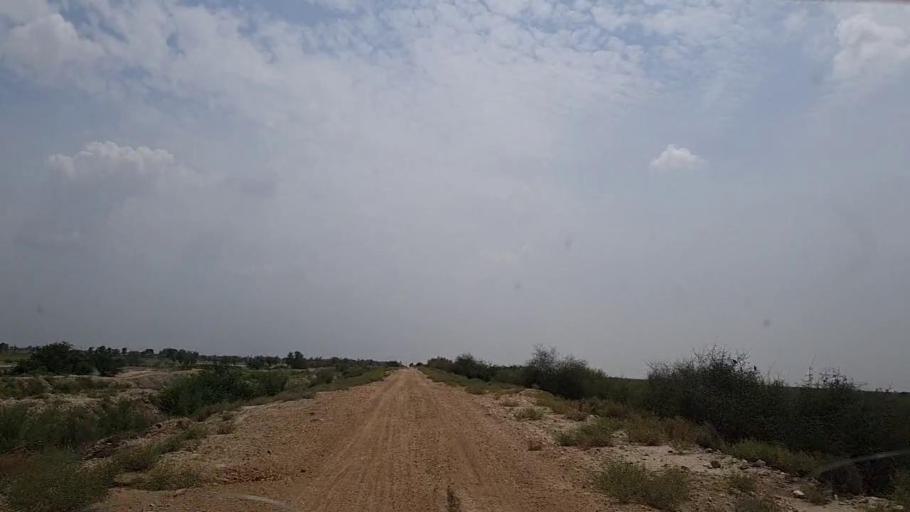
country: PK
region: Sindh
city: Phulji
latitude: 26.8196
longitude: 67.6116
